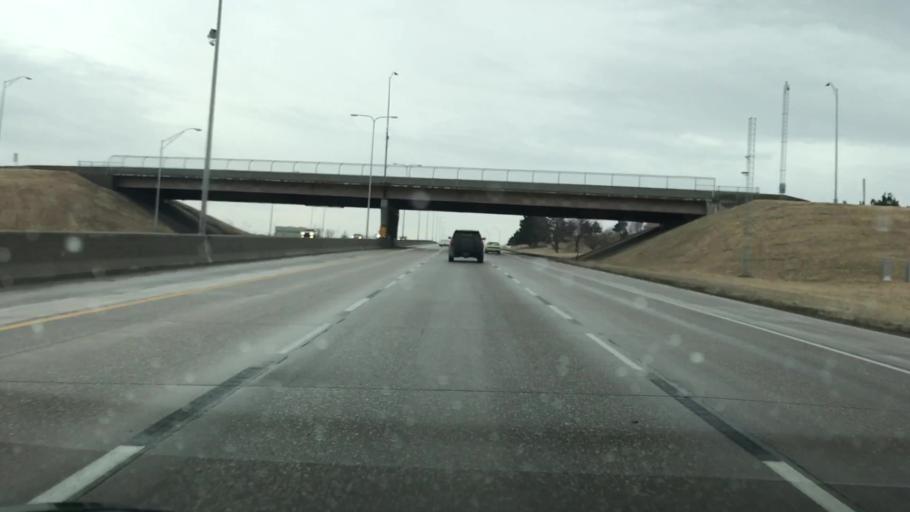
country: US
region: Nebraska
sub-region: Sarpy County
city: Chalco
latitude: 41.1859
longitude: -96.1082
